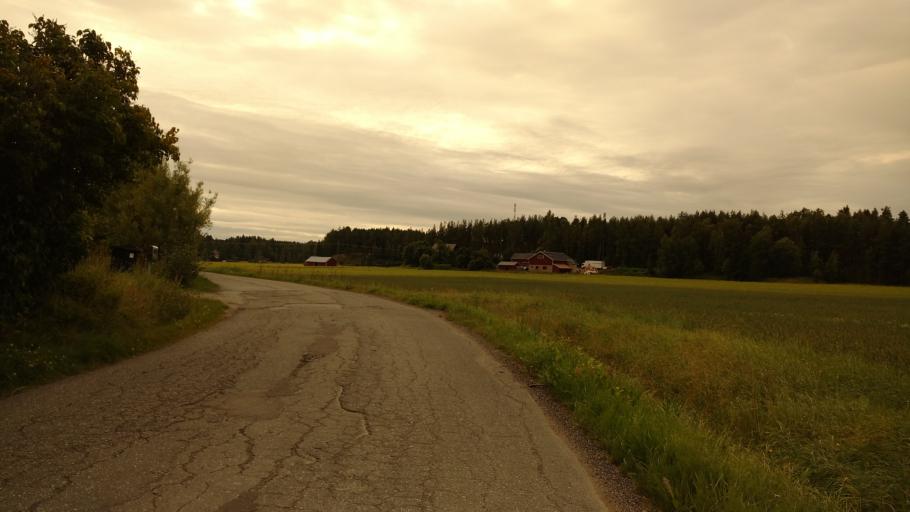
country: FI
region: Varsinais-Suomi
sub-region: Turku
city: Piikkioe
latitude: 60.4298
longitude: 22.4601
